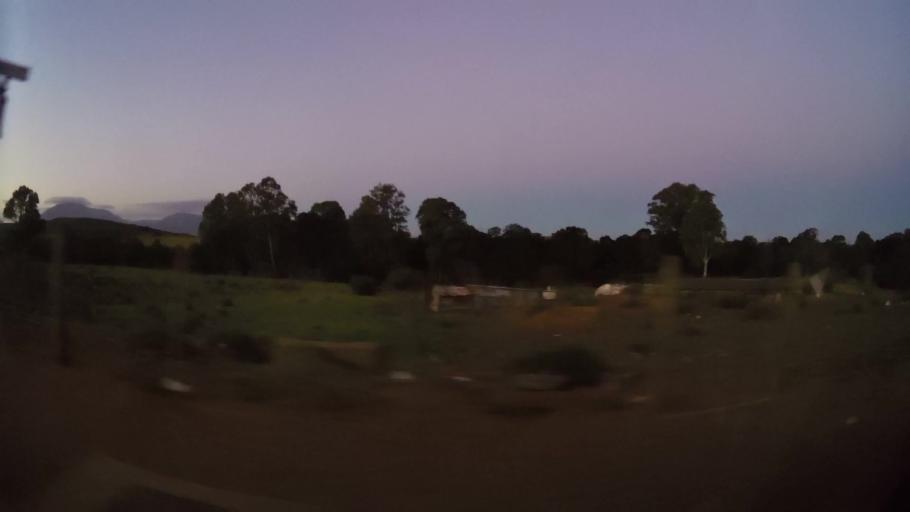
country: ZA
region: Western Cape
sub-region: Eden District Municipality
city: Riversdale
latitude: -34.1041
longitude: 21.2742
